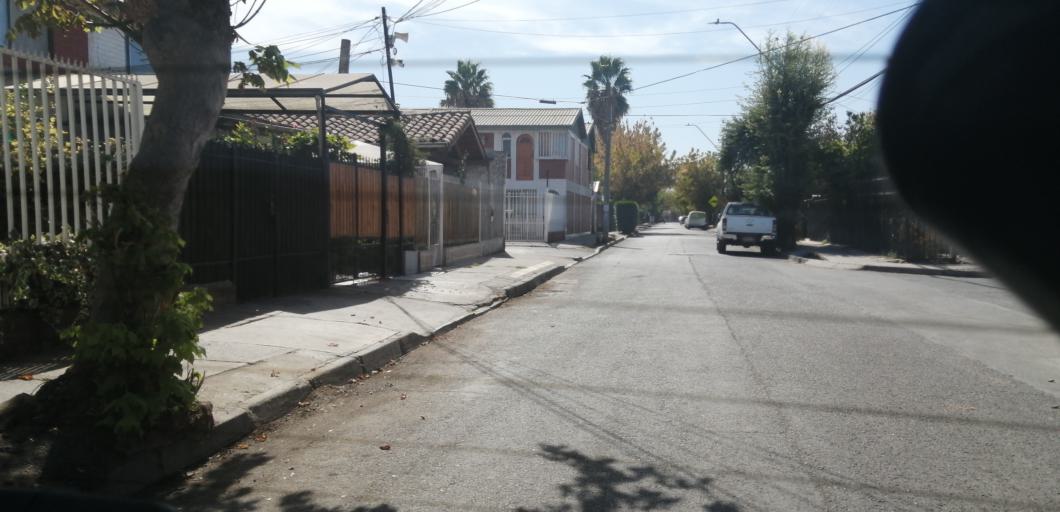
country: CL
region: Santiago Metropolitan
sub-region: Provincia de Santiago
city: Lo Prado
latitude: -33.4636
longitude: -70.7322
